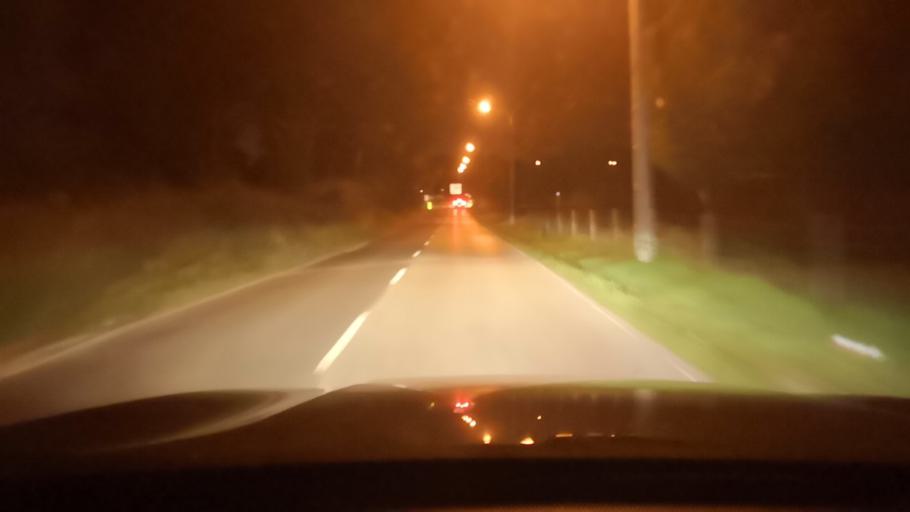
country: PT
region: Setubal
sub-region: Setubal
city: Setubal
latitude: 38.5441
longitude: -8.8584
